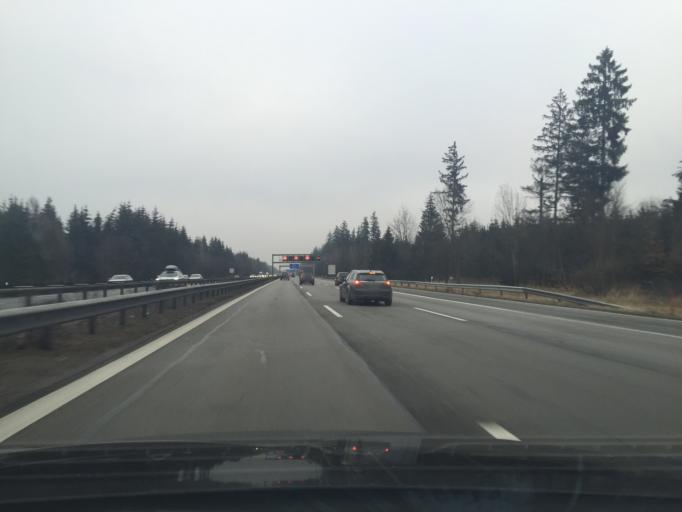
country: DE
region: Bavaria
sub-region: Upper Bavaria
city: Sauerlach
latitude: 47.9639
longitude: 11.6885
